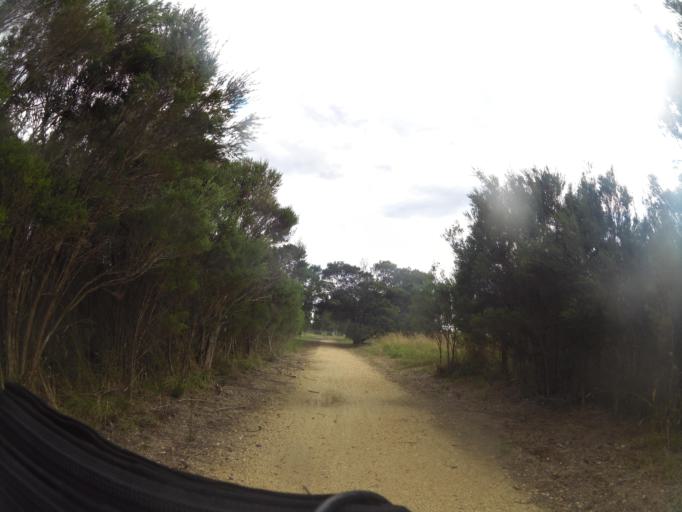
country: AU
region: Victoria
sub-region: Latrobe
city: Traralgon
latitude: -38.0533
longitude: 146.6281
